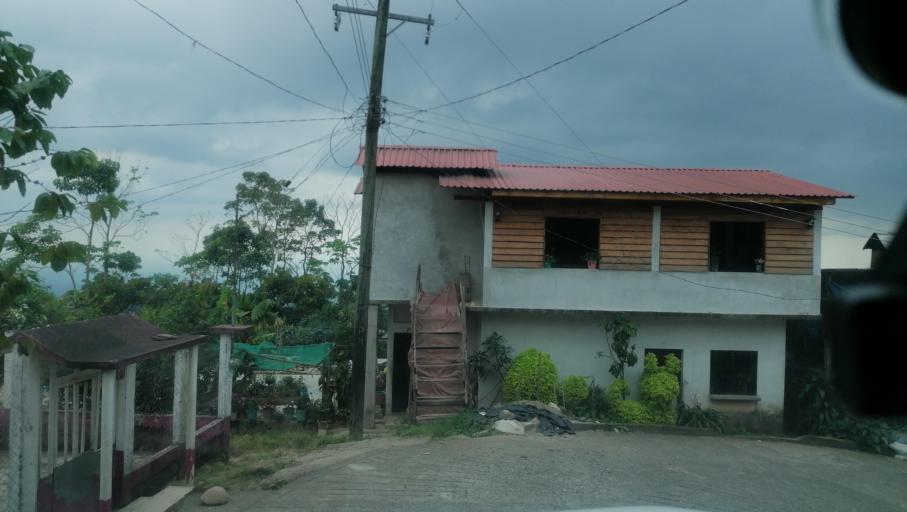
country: MX
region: Chiapas
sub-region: Cacahoatan
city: Benito Juarez
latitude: 15.0827
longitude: -92.1617
